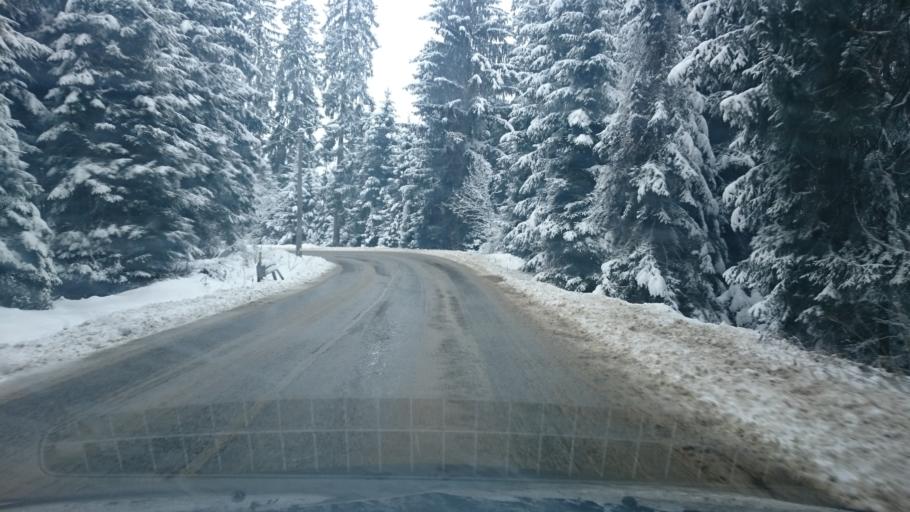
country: BA
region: Republika Srpska
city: Skender Vakuf
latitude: 44.4975
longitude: 17.3699
